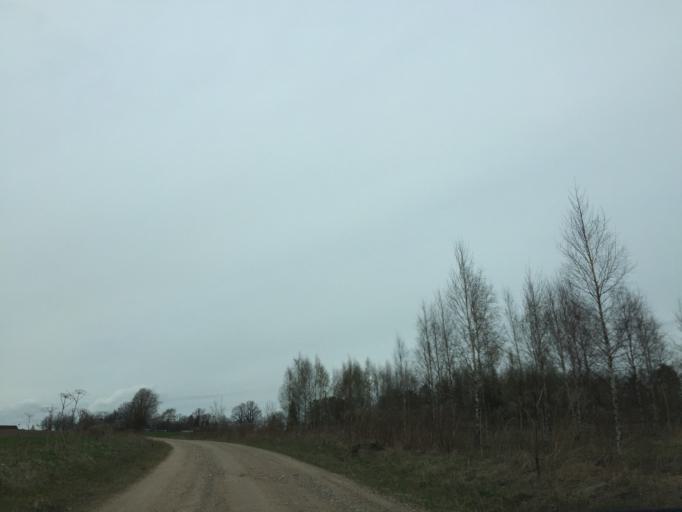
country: LV
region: Priekuli
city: Priekuli
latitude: 57.3362
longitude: 25.3751
